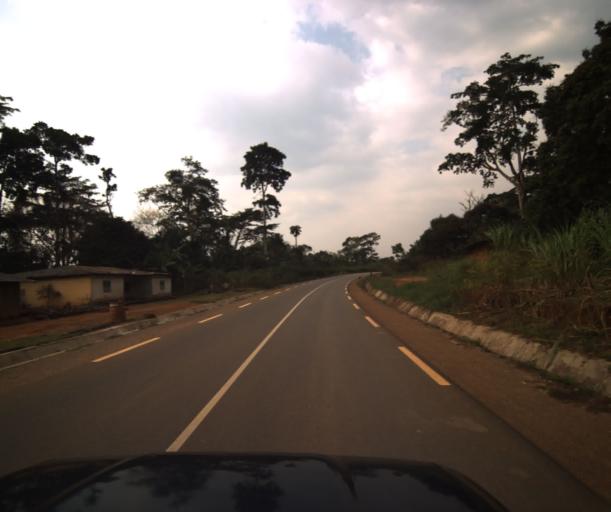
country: CM
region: Centre
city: Mbankomo
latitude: 3.7493
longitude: 11.4017
